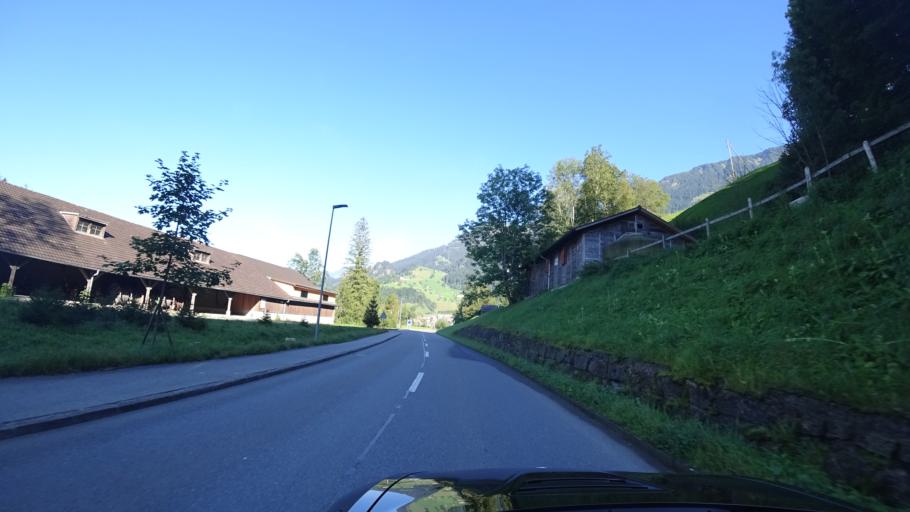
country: CH
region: Obwalden
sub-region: Obwalden
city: Giswil
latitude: 46.8296
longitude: 8.1681
